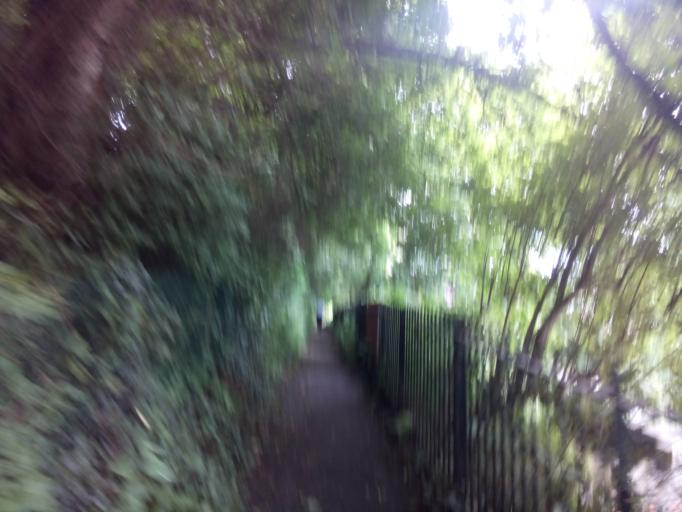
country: GB
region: England
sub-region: County Durham
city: Durham
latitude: 54.7737
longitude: -1.5734
